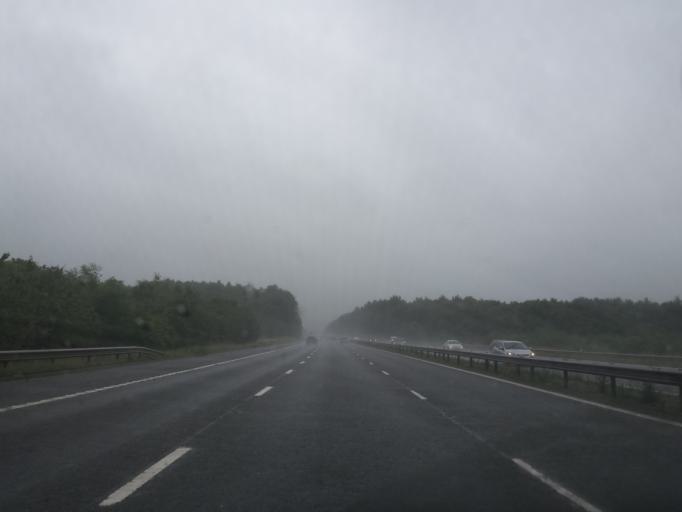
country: GB
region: England
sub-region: Leicestershire
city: Markfield
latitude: 52.6608
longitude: -1.2609
